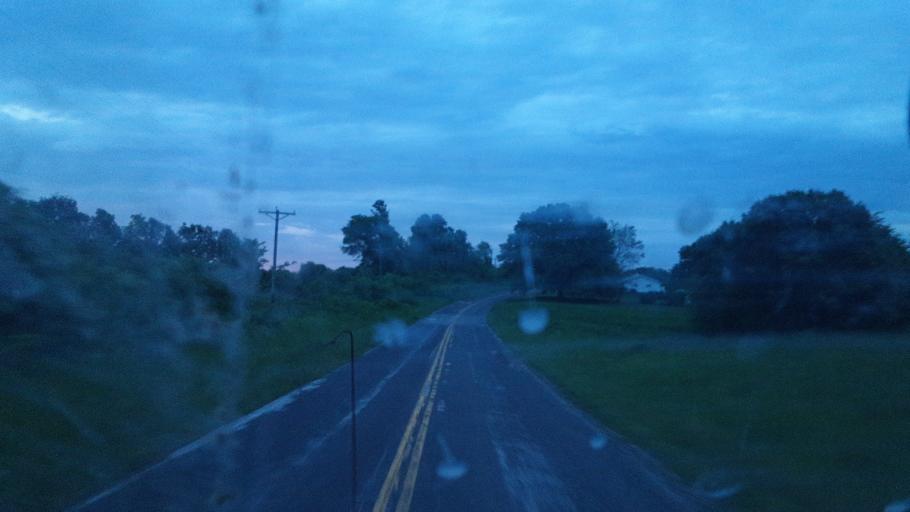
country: US
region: Missouri
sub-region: Clark County
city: Kahoka
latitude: 40.4344
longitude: -91.5880
